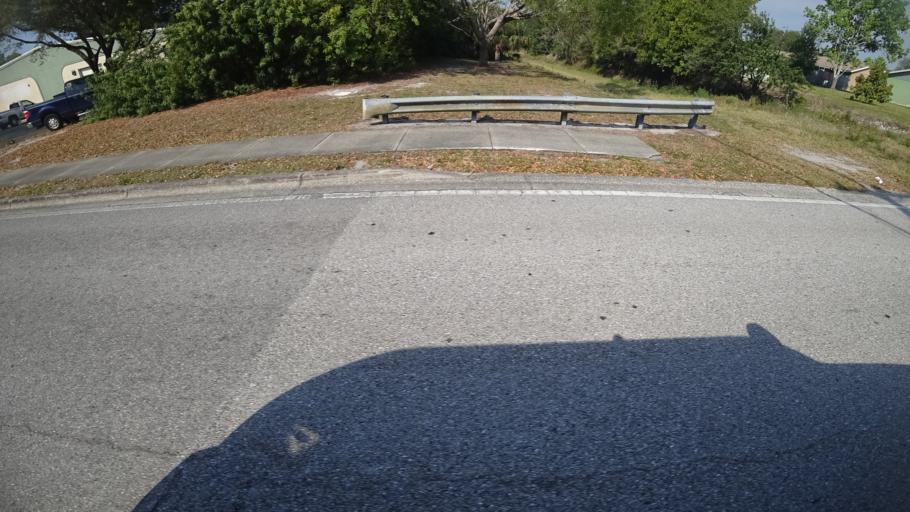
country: US
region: Florida
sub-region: Manatee County
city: Whitfield
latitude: 27.4090
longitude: -82.5551
